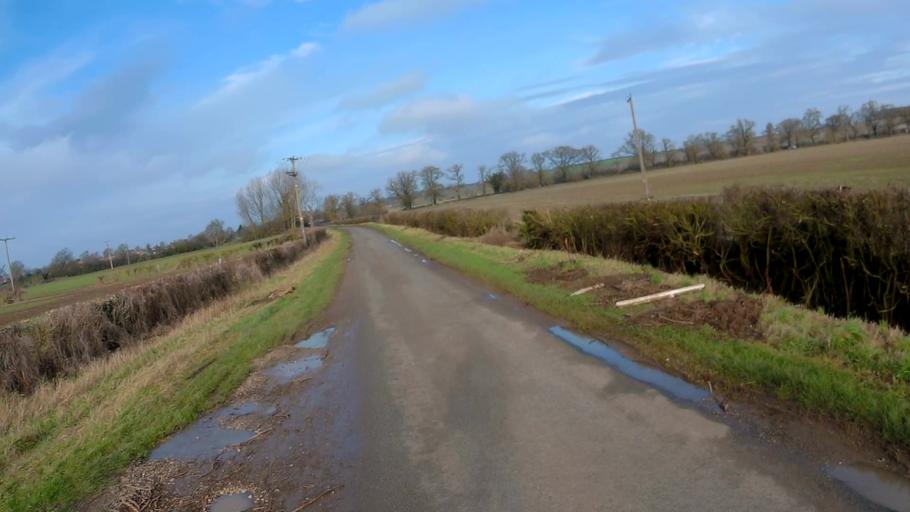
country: GB
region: England
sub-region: Lincolnshire
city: Bourne
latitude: 52.7742
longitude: -0.4259
